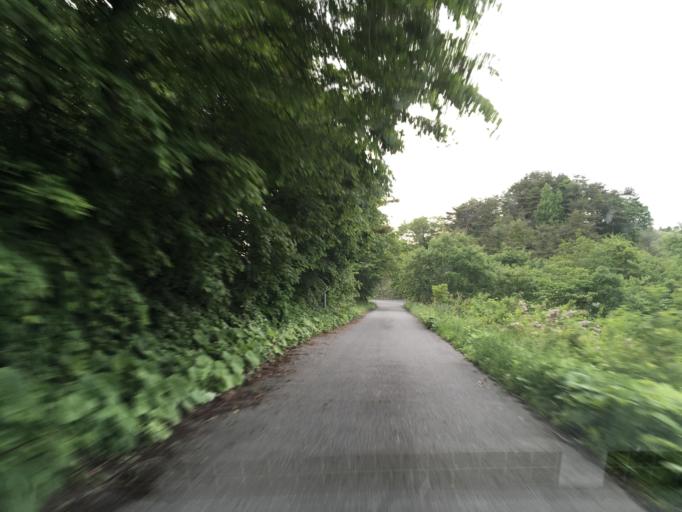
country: JP
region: Iwate
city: Mizusawa
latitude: 39.1356
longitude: 141.3133
